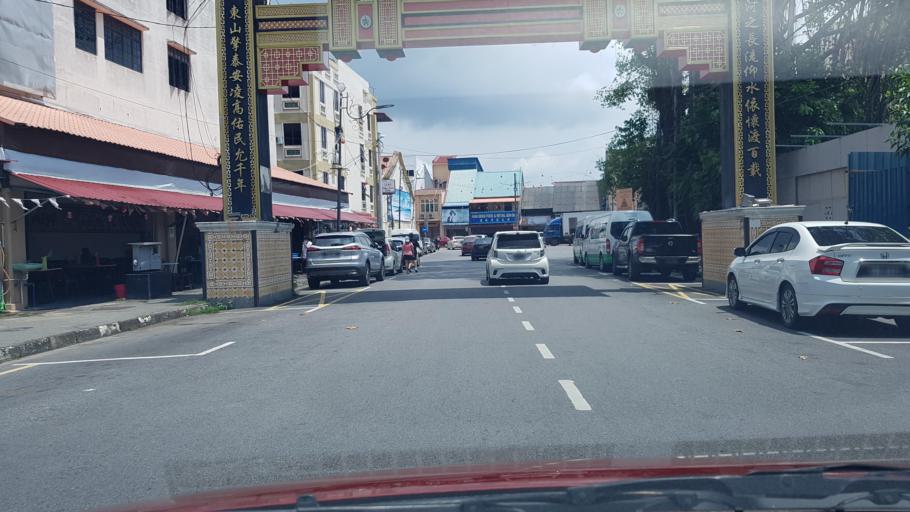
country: MY
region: Terengganu
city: Kuala Terengganu
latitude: 5.3322
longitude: 103.1337
